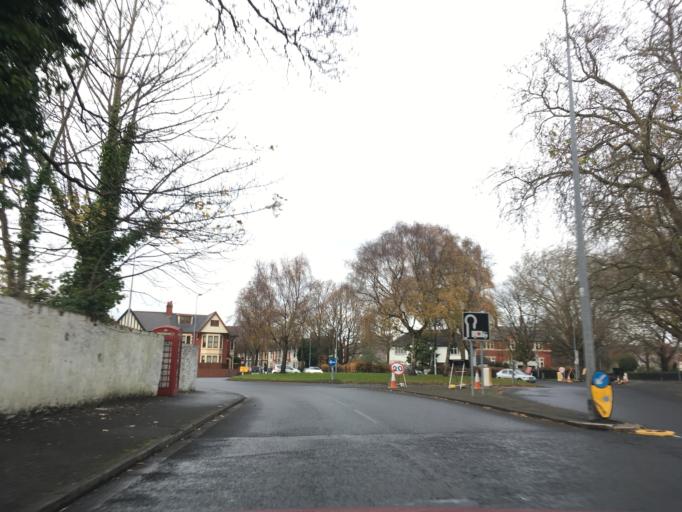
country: GB
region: Wales
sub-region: Cardiff
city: Cardiff
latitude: 51.4921
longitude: -3.1551
